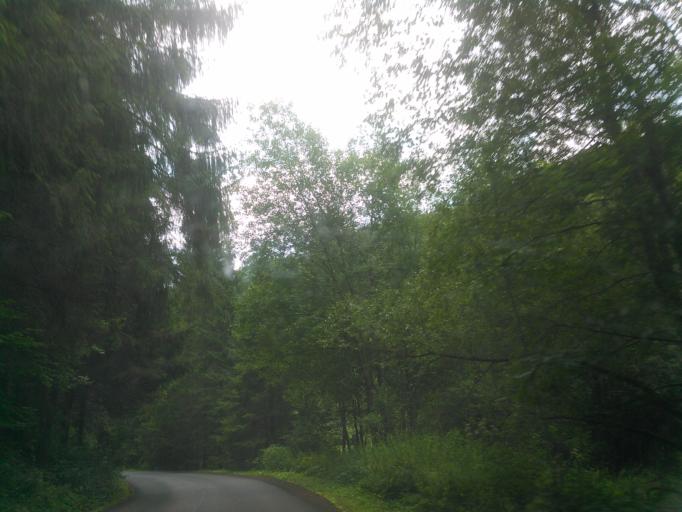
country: SK
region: Zilinsky
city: Ruzomberok
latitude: 49.0417
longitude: 19.4181
